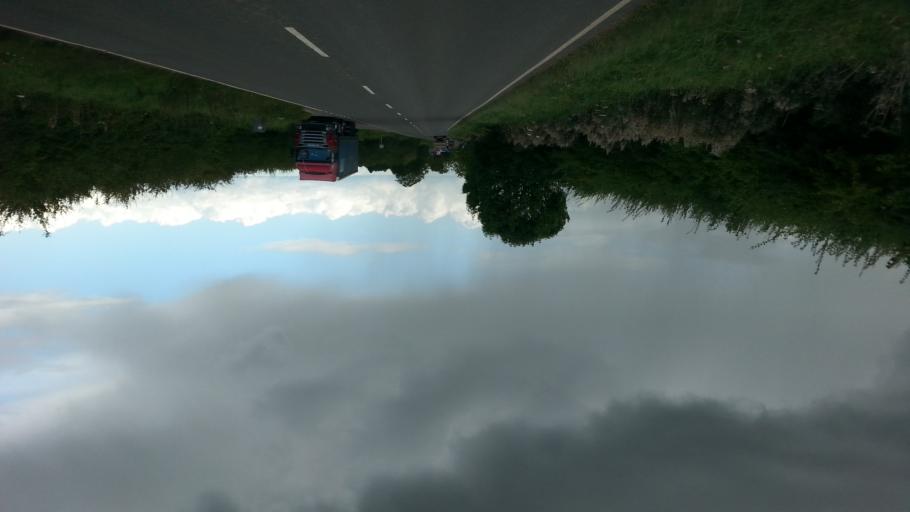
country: GB
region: England
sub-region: Cambridgeshire
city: Godmanchester
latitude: 52.3017
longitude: -0.1571
